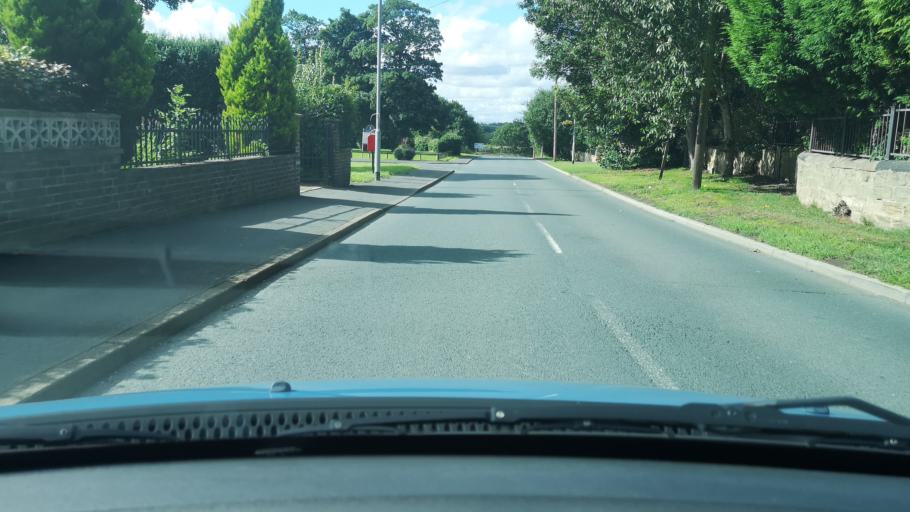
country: GB
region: England
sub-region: City and Borough of Wakefield
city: Featherstone
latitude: 53.6918
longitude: -1.3775
